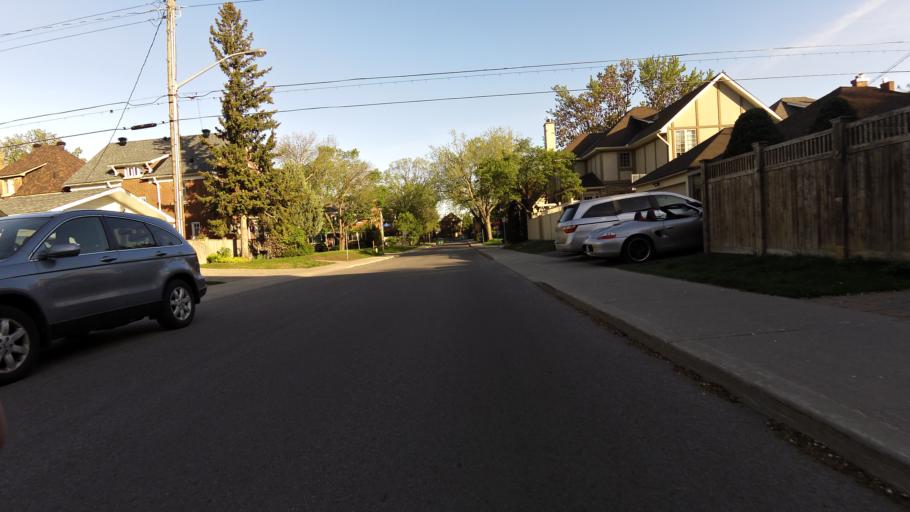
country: CA
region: Ontario
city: Ottawa
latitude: 45.3997
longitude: -75.6962
